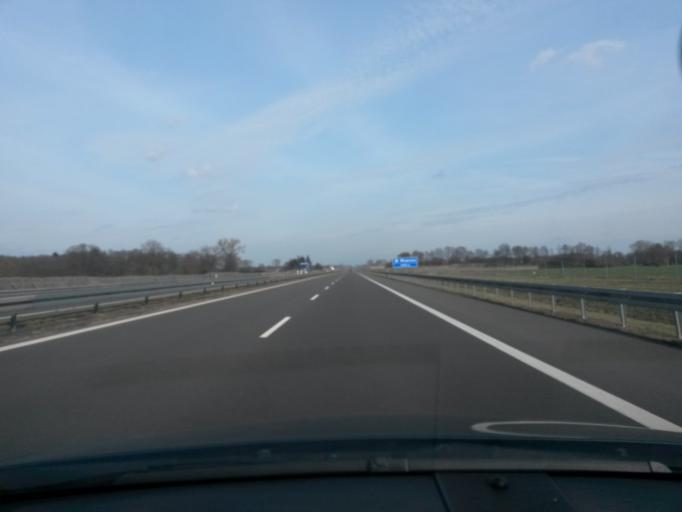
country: PL
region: Greater Poland Voivodeship
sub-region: Powiat wrzesinski
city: Nekla
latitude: 52.3184
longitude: 17.4806
